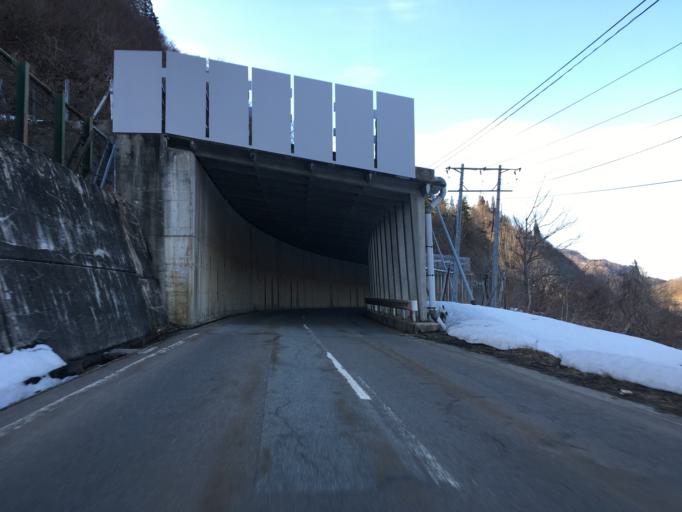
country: JP
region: Yamagata
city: Nagai
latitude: 37.9538
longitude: 139.9167
